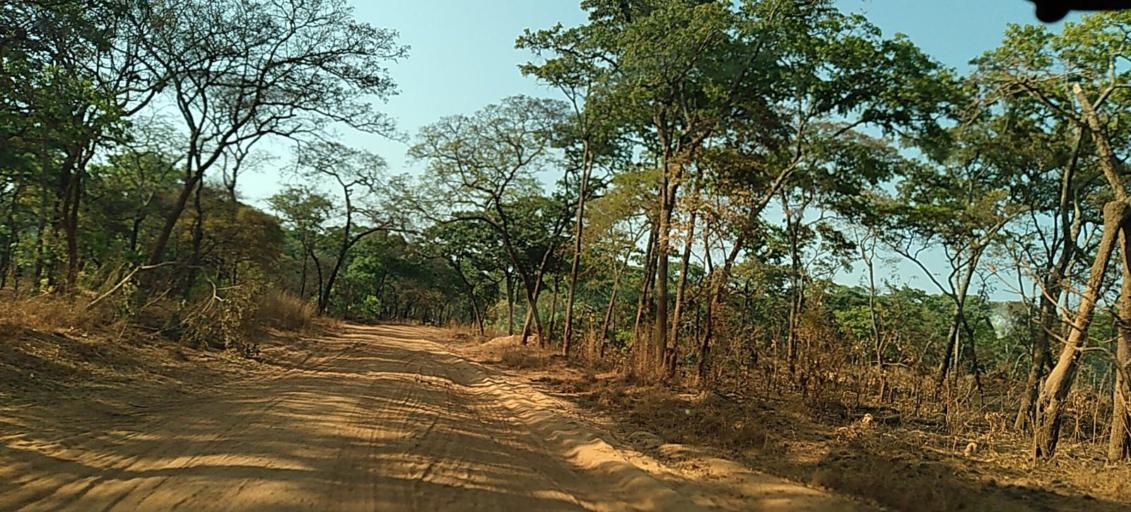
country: ZM
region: North-Western
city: Kasempa
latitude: -13.5573
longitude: 25.9997
